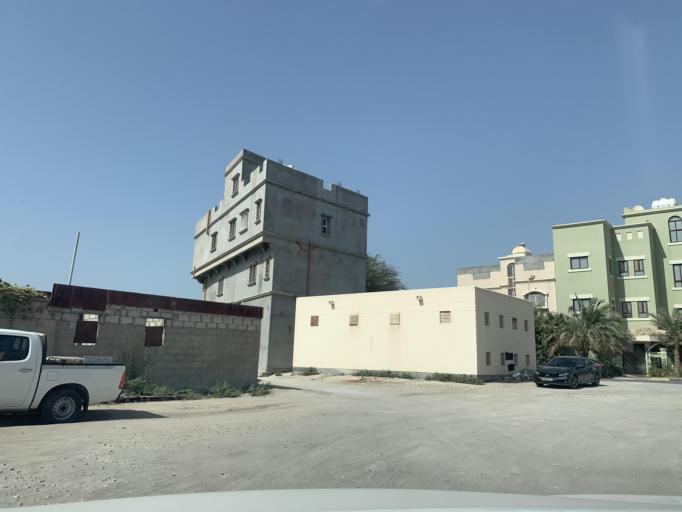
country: BH
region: Manama
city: Jidd Hafs
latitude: 26.2331
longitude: 50.4801
